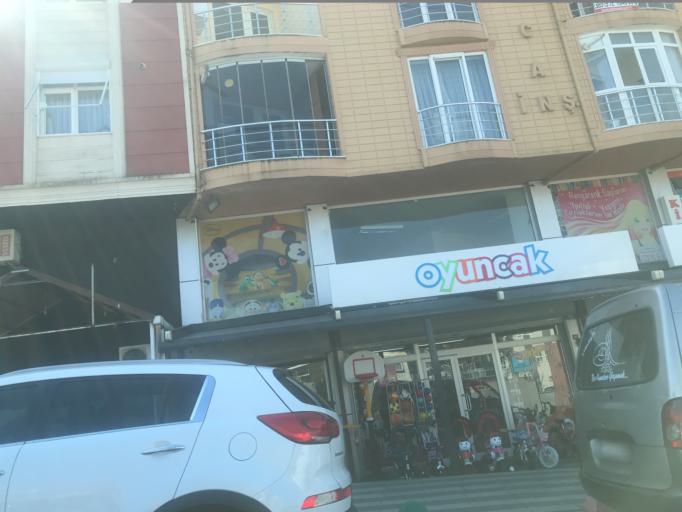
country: TR
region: Istanbul
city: Samandira
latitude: 41.0331
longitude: 29.1811
